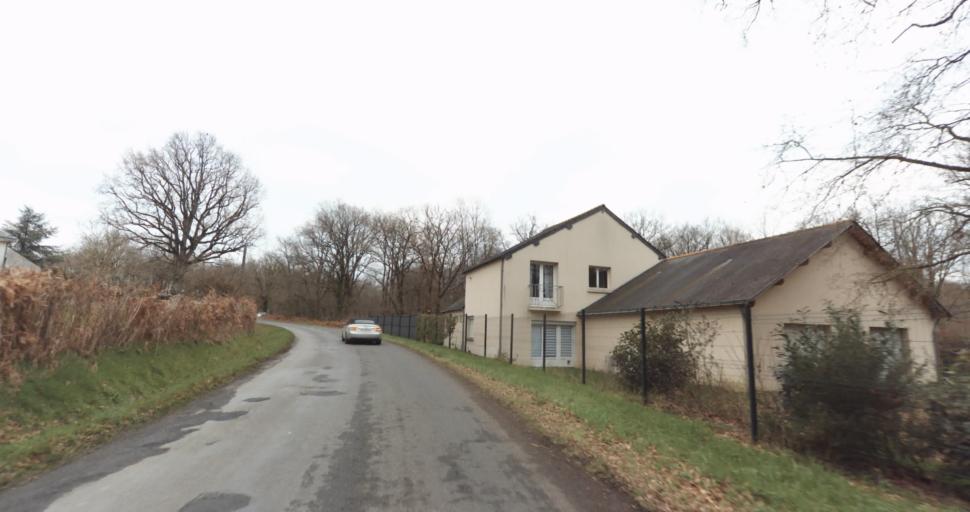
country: FR
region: Pays de la Loire
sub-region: Departement de Maine-et-Loire
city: Distre
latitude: 47.2547
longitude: -0.1249
